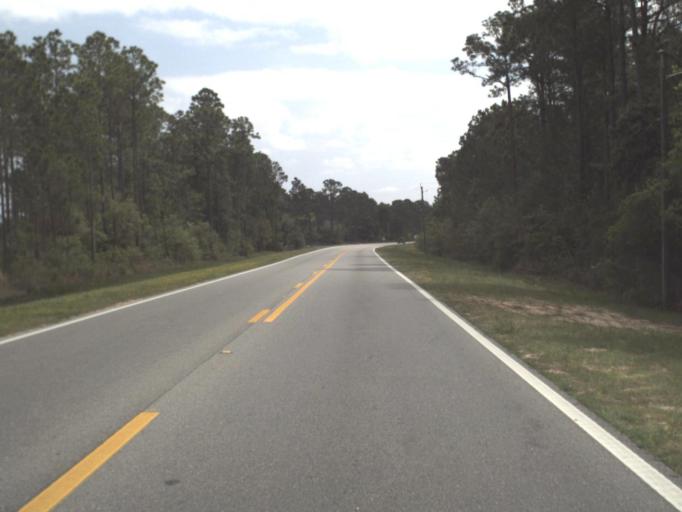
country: US
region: Florida
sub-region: Escambia County
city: Myrtle Grove
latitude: 30.3480
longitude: -87.3918
